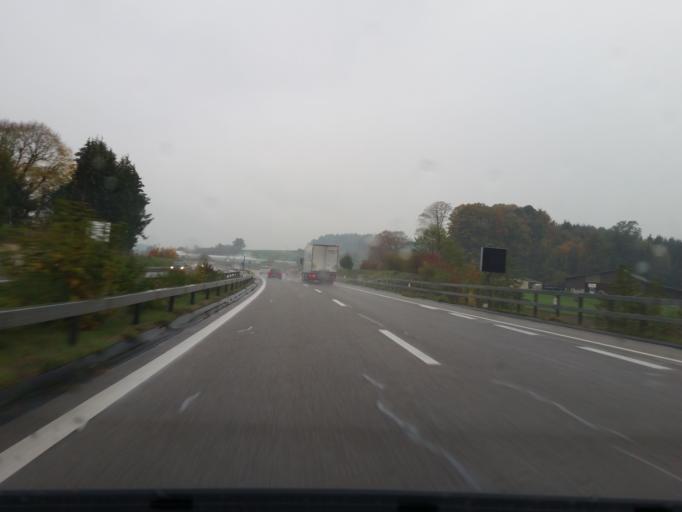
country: CH
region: Thurgau
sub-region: Frauenfeld District
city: Gachnang
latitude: 47.5522
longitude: 8.8313
